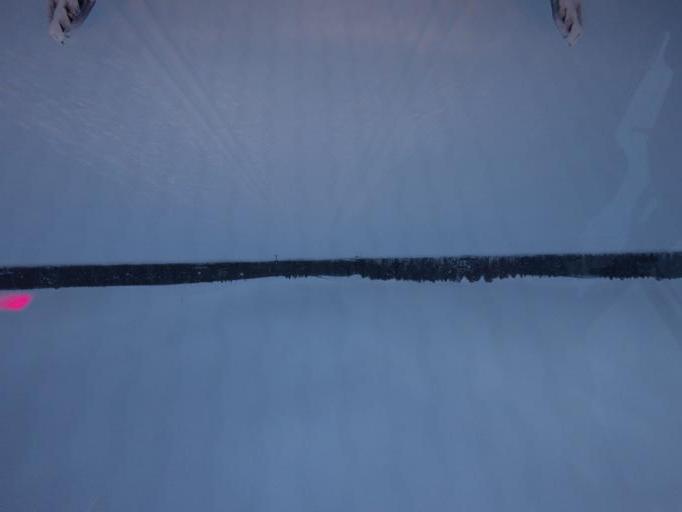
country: FI
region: Lapland
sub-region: Tunturi-Lappi
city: Kolari
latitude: 67.6088
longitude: 24.1680
